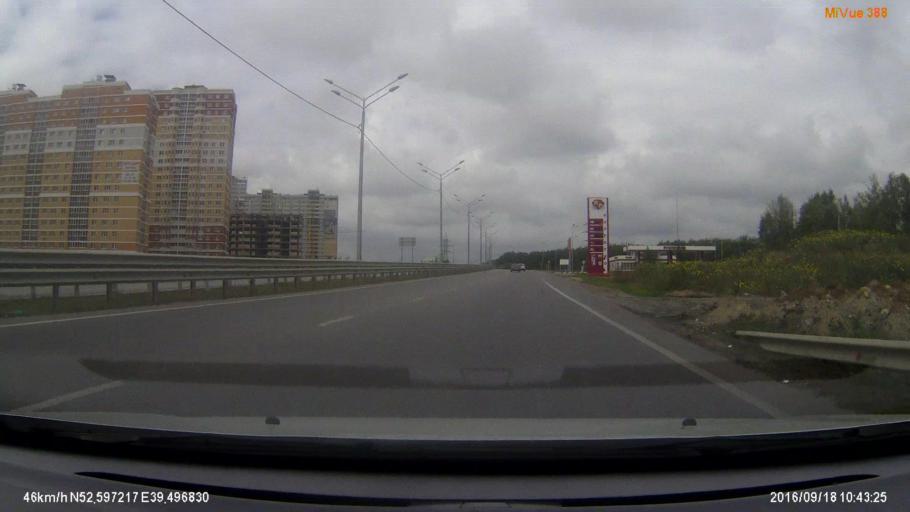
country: RU
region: Lipetsk
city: Syrskoye
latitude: 52.5972
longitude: 39.4975
